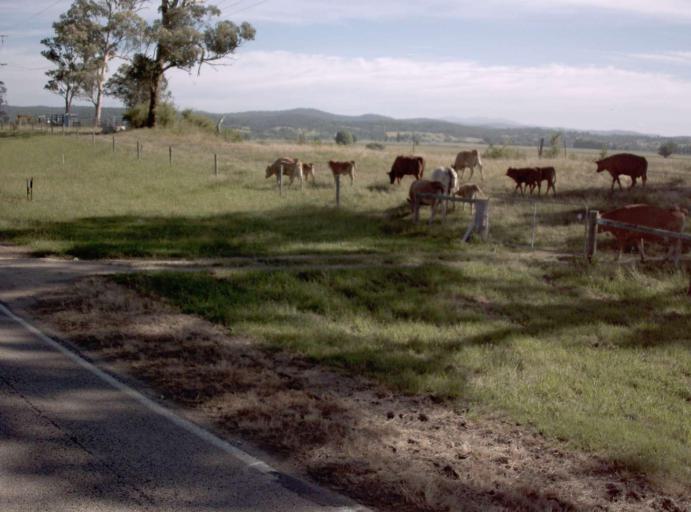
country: AU
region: Victoria
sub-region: East Gippsland
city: Bairnsdale
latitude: -37.7363
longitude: 147.8125
